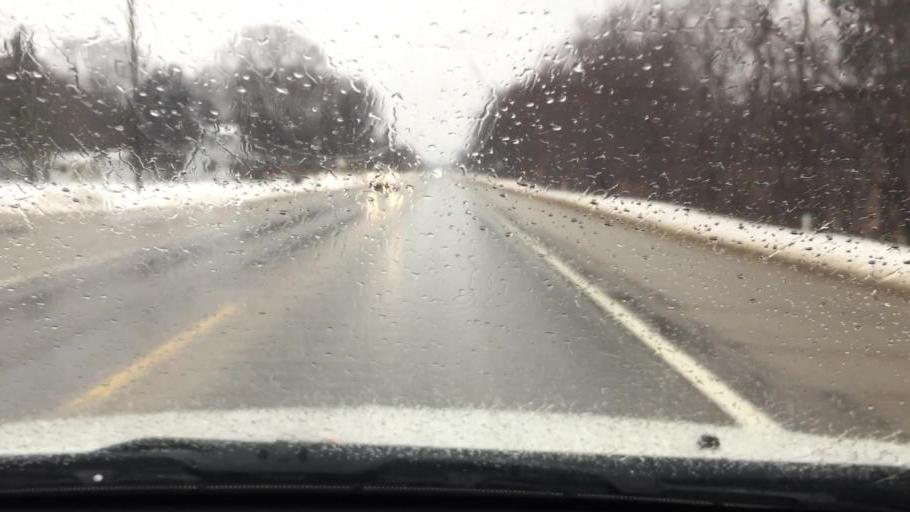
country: US
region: Michigan
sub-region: Charlevoix County
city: Charlevoix
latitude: 45.2853
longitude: -85.2419
